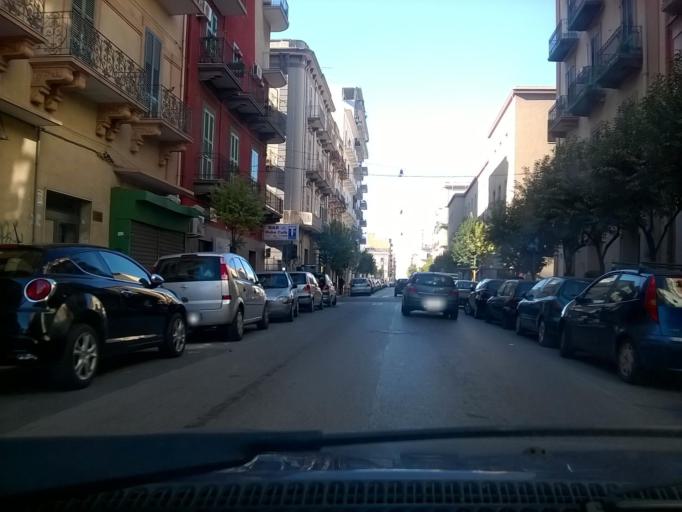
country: IT
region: Apulia
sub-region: Provincia di Taranto
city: Taranto
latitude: 40.4650
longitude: 17.2515
